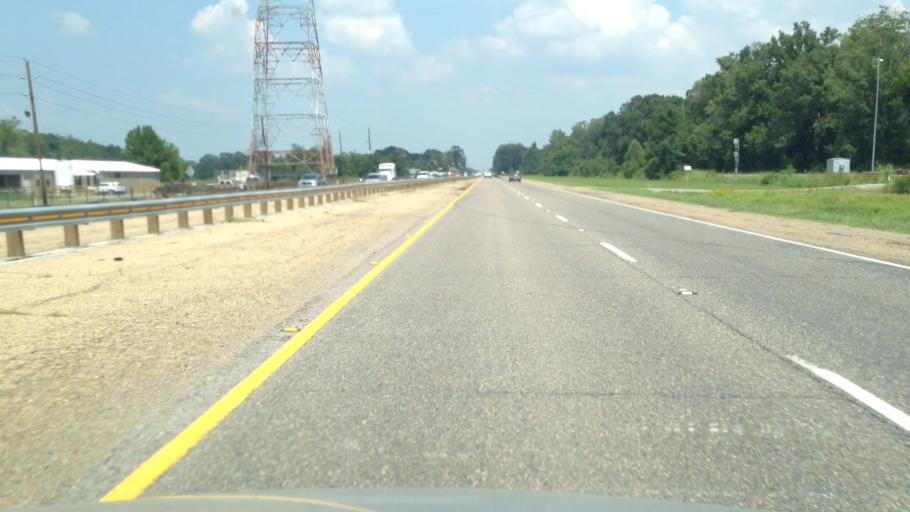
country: US
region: Louisiana
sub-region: Pointe Coupee Parish
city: Livonia
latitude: 30.5551
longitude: -91.5747
